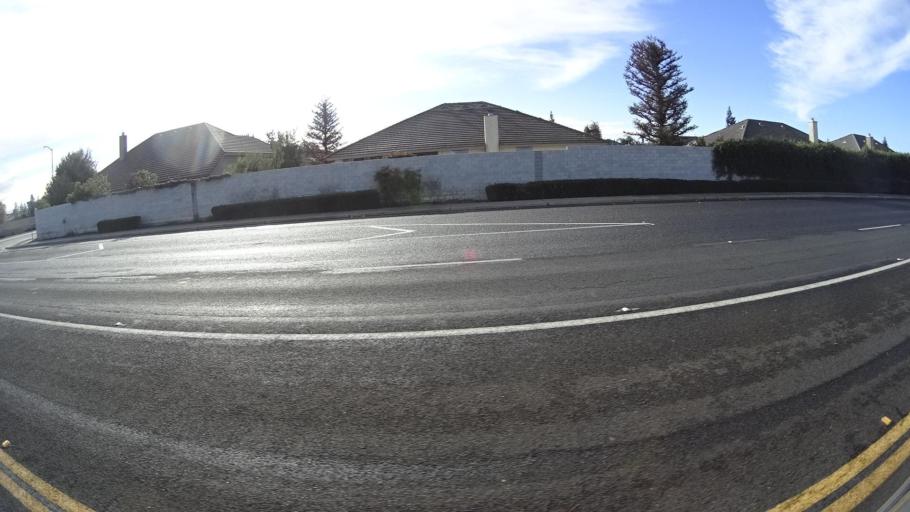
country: US
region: California
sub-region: Kern County
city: Rosedale
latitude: 35.3835
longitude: -119.1725
